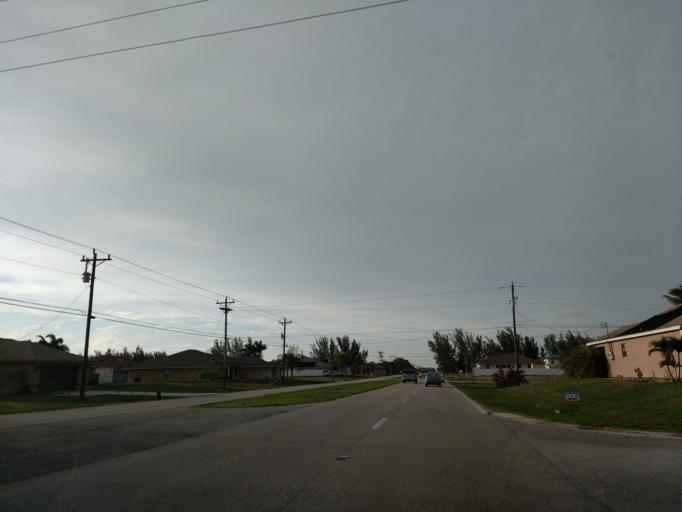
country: US
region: Florida
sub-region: Lee County
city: Cape Coral
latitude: 26.5966
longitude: -82.0069
